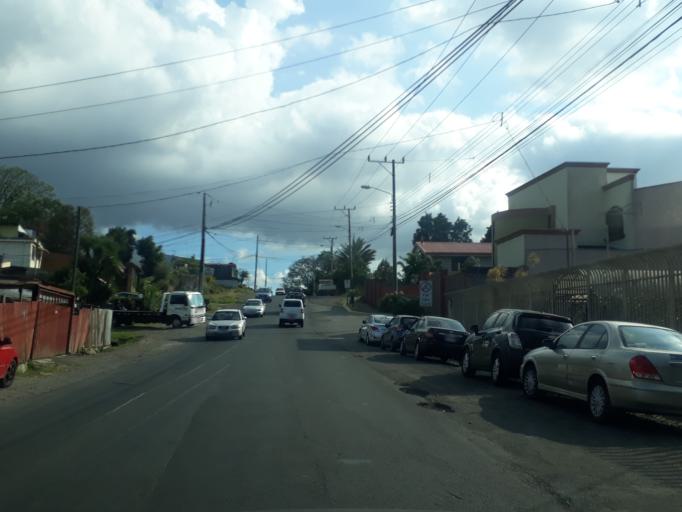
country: CR
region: San Jose
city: Purral
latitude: 9.9709
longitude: -84.0337
